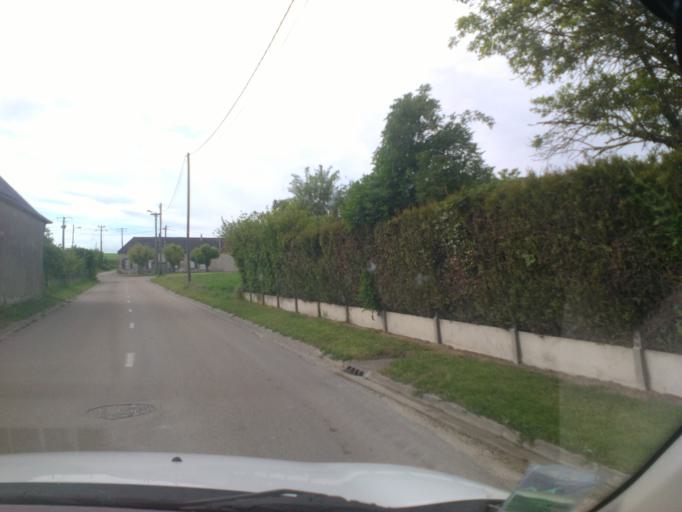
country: FR
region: Champagne-Ardenne
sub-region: Departement de l'Aube
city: Marigny-le-Chatel
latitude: 48.3523
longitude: 3.6552
